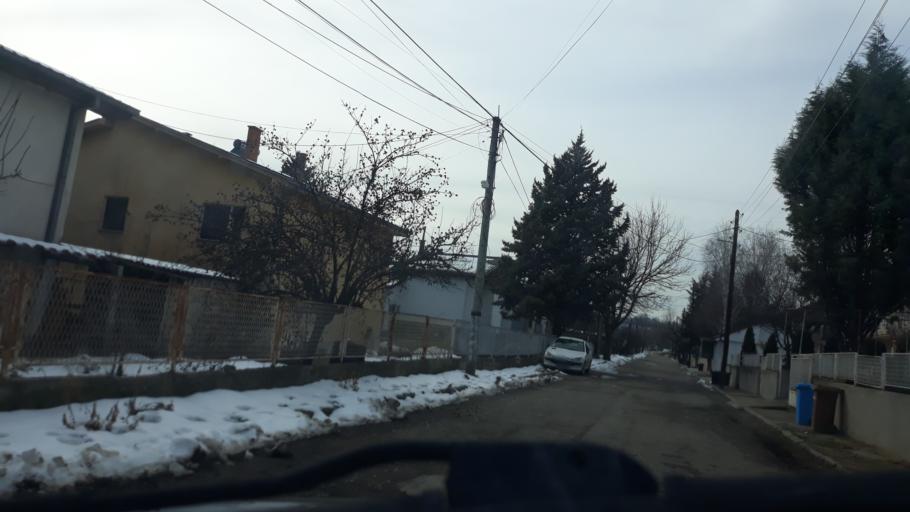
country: MK
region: Negotino
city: Negotino
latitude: 41.4830
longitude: 22.0823
